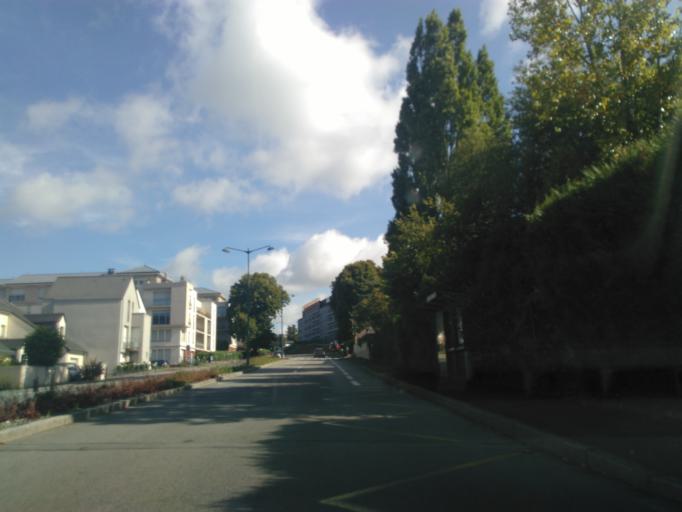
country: FR
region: Brittany
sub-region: Departement d'Ille-et-Vilaine
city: Rennes
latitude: 48.1358
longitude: -1.6593
